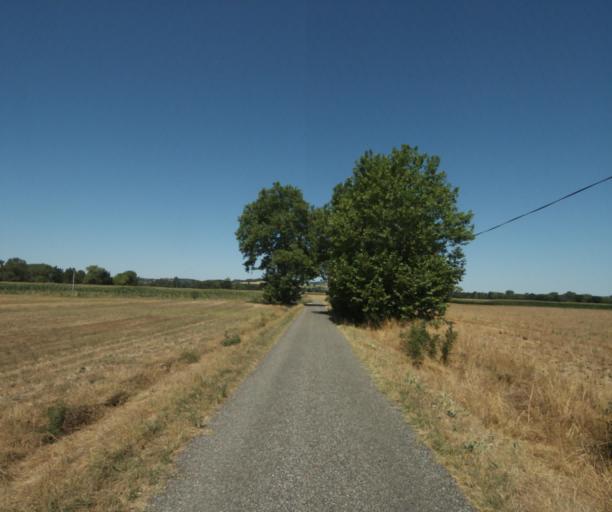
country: FR
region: Midi-Pyrenees
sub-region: Departement de la Haute-Garonne
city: Revel
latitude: 43.4853
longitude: 1.9660
